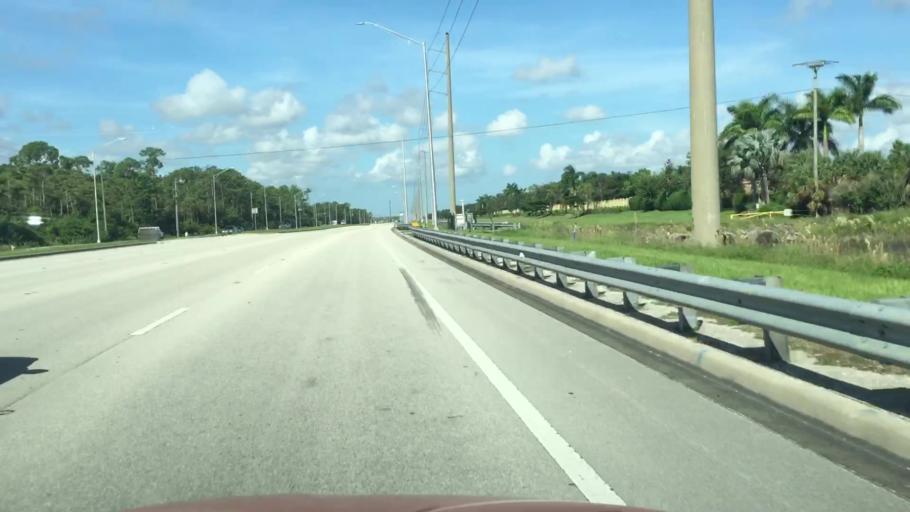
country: US
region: Florida
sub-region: Collier County
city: Vineyards
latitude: 26.2733
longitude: -81.6564
